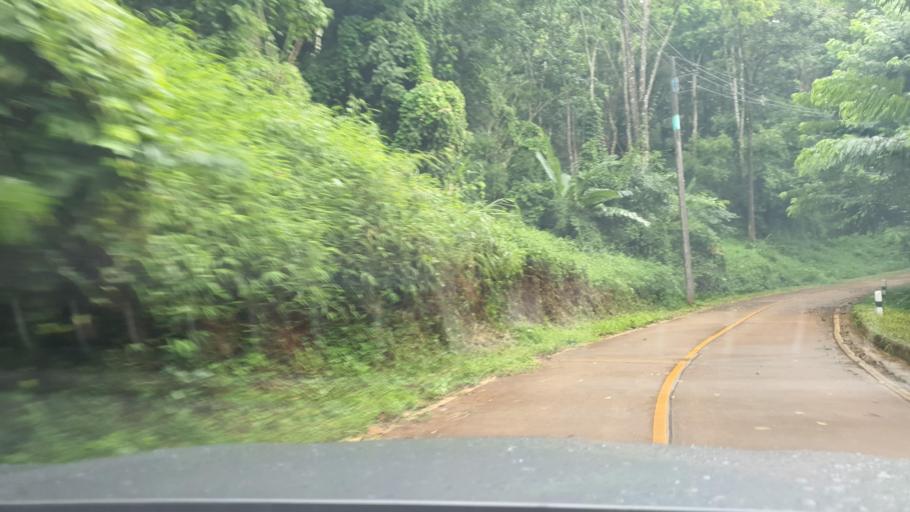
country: TH
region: Chiang Mai
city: Samoeng
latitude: 18.8352
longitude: 98.7786
